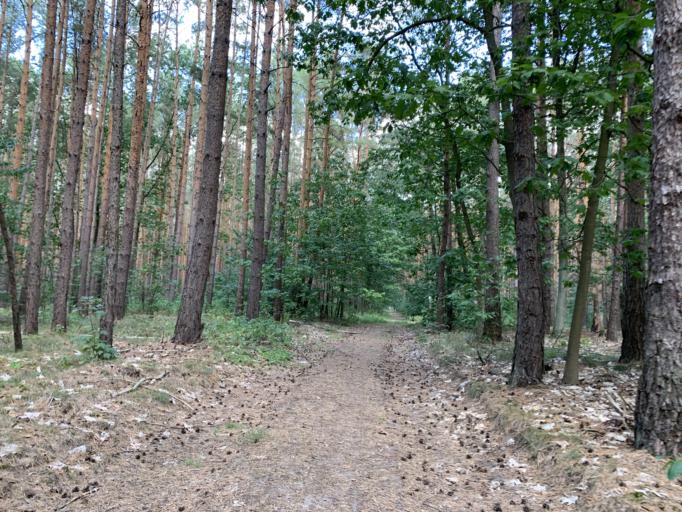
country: DE
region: Brandenburg
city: Michendorf
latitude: 52.3170
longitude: 13.0072
